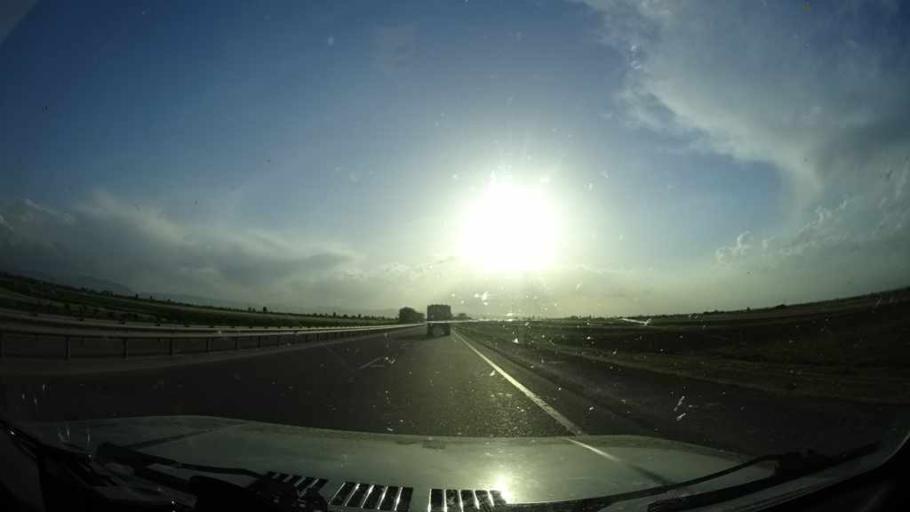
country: AZ
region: Samux
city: Samux
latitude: 40.6895
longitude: 46.5299
